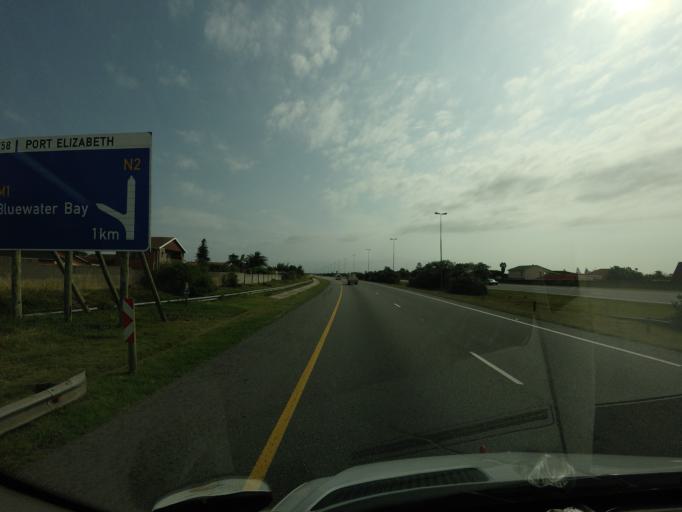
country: ZA
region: Eastern Cape
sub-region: Nelson Mandela Bay Metropolitan Municipality
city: Port Elizabeth
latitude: -33.8612
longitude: 25.6299
